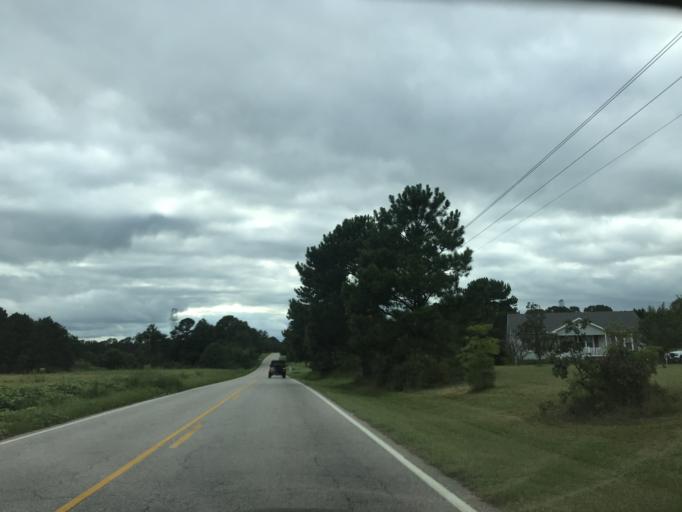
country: US
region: North Carolina
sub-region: Johnston County
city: Clayton
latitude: 35.5726
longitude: -78.5603
